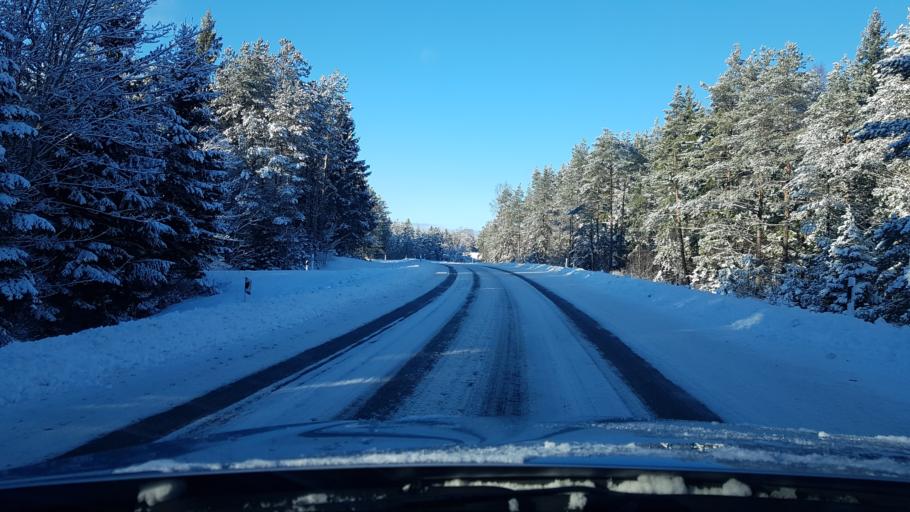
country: EE
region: Hiiumaa
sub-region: Kaerdla linn
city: Kardla
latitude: 58.9726
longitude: 22.7669
